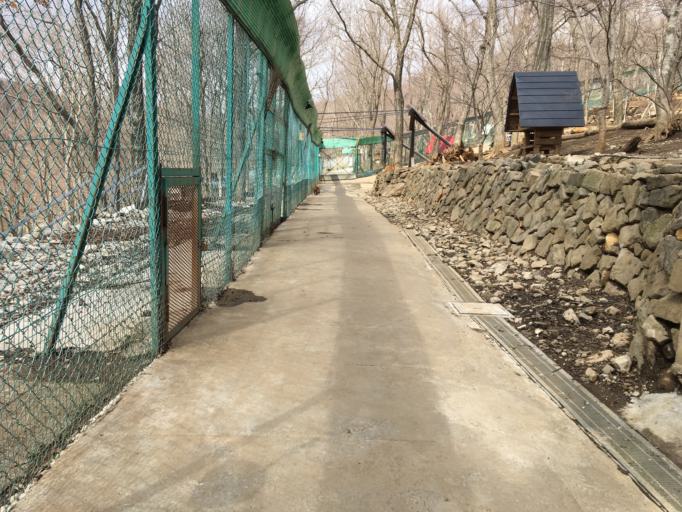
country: JP
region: Miyagi
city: Shiroishi
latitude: 38.0413
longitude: 140.5305
